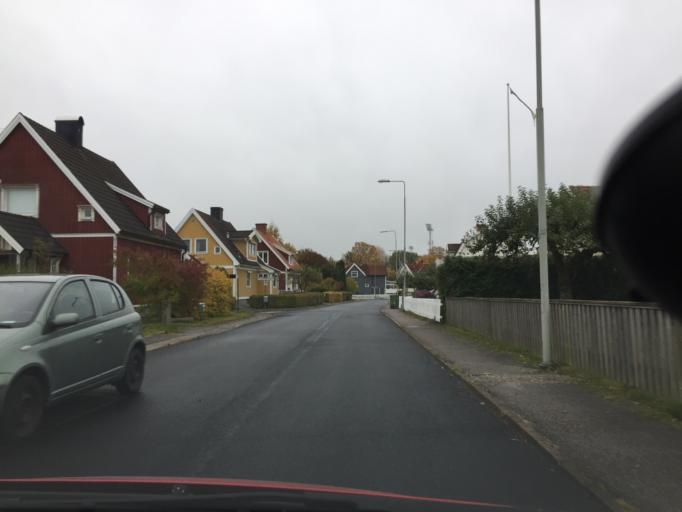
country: SE
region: Vaestra Goetaland
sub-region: Trollhattan
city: Trollhattan
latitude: 58.2925
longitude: 12.3070
